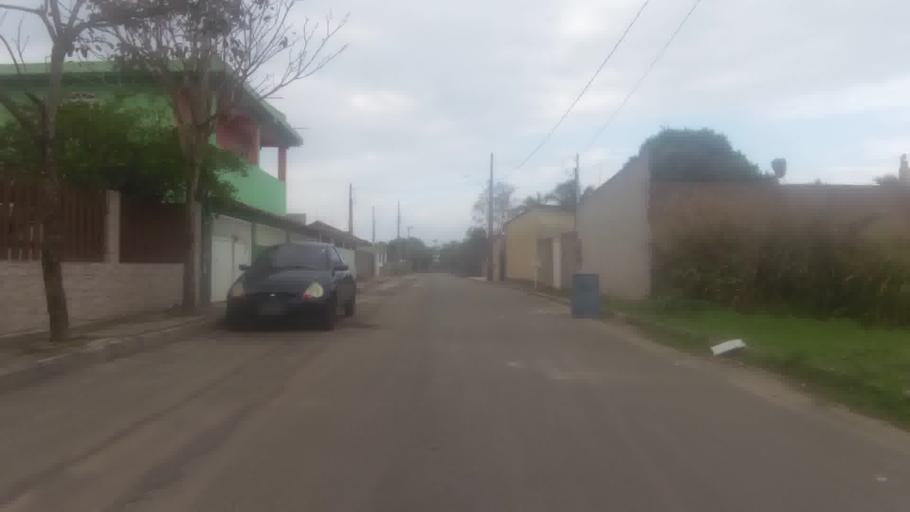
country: BR
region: Espirito Santo
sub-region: Piuma
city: Piuma
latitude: -20.7990
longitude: -40.5876
